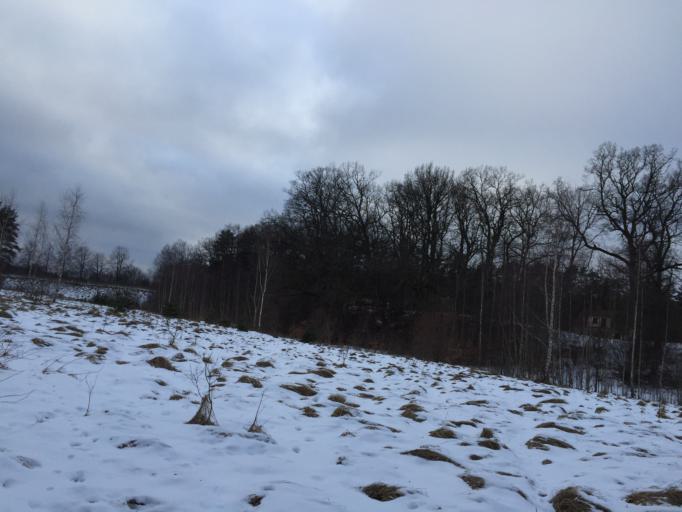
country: LV
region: Seja
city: Loja
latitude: 57.1308
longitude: 24.6661
